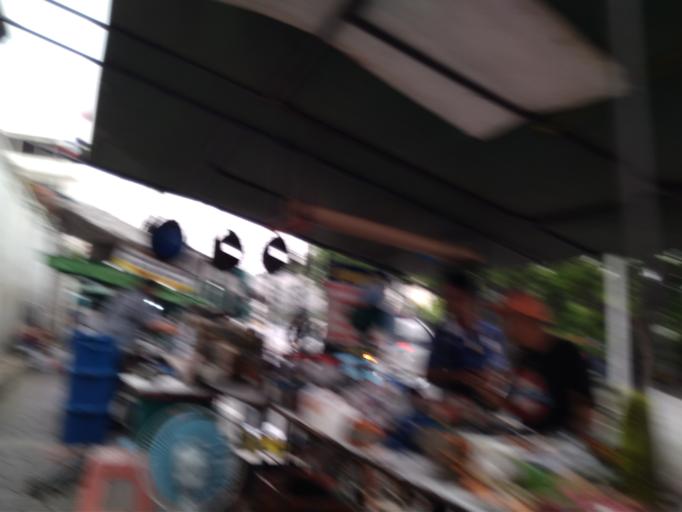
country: TH
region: Bangkok
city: Bangkok
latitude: 13.7461
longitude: 100.4965
